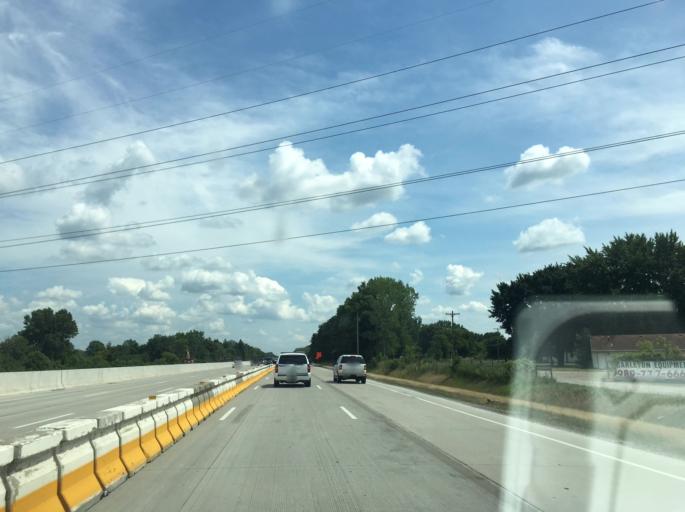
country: US
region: Michigan
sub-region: Saginaw County
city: Buena Vista
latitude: 43.3934
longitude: -83.8873
